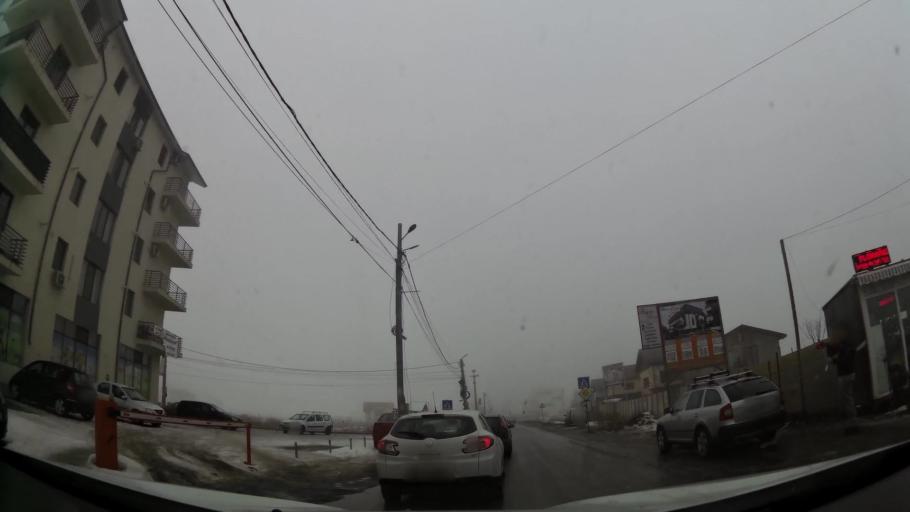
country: RO
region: Ilfov
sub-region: Comuna Chiajna
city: Chiajna
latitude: 44.4501
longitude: 25.9817
